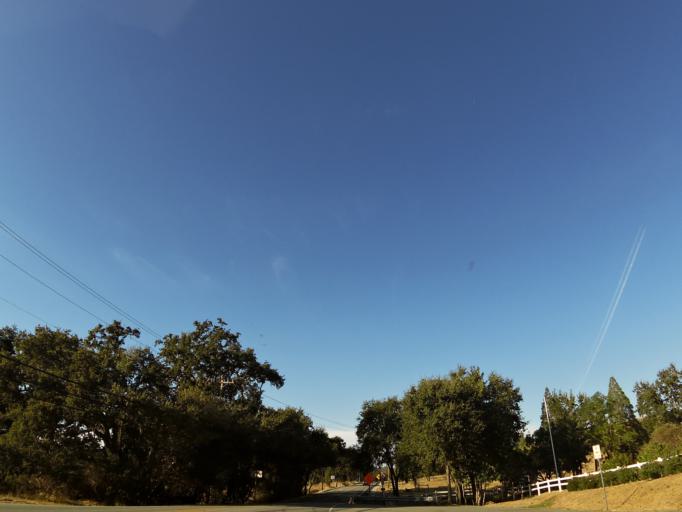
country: US
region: California
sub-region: Santa Clara County
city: San Martin
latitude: 37.0596
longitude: -121.6629
